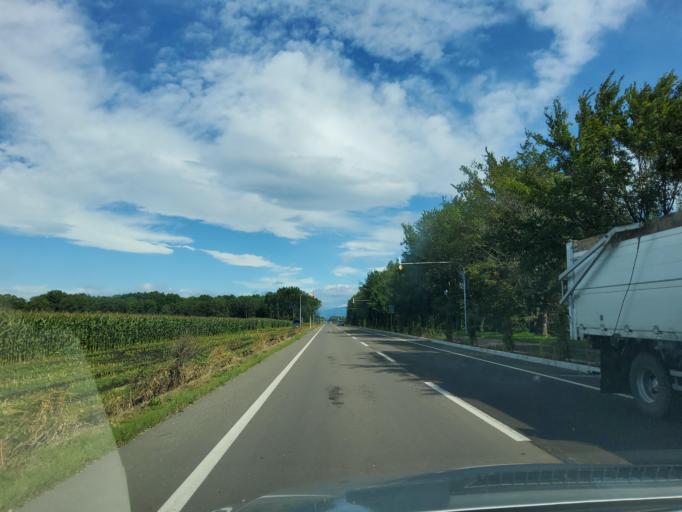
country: JP
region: Hokkaido
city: Otofuke
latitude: 42.9826
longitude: 143.1767
